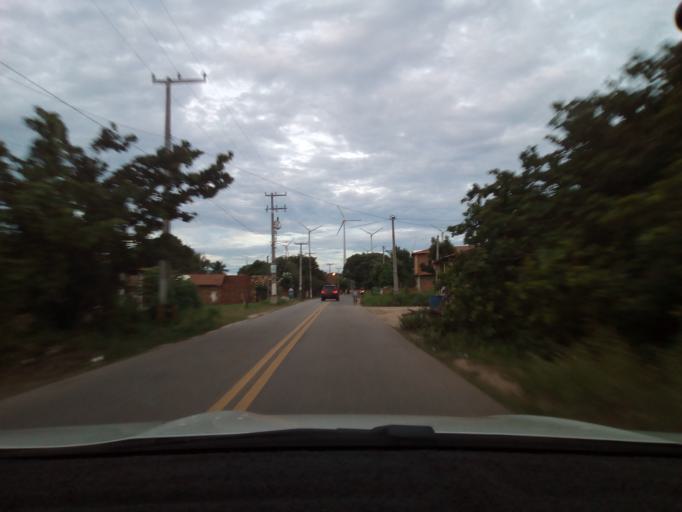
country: BR
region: Ceara
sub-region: Beberibe
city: Beberibe
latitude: -4.1843
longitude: -38.0959
